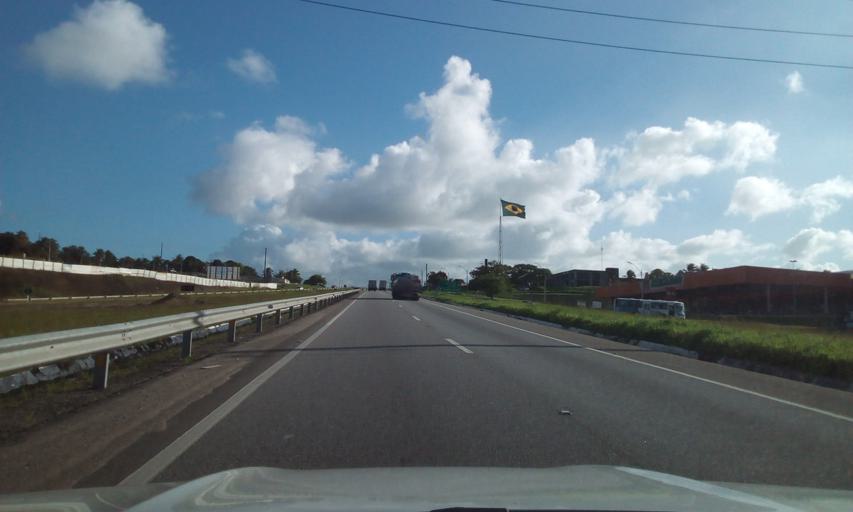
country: BR
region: Paraiba
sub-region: Bayeux
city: Bayeux
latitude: -7.1242
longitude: -34.9467
